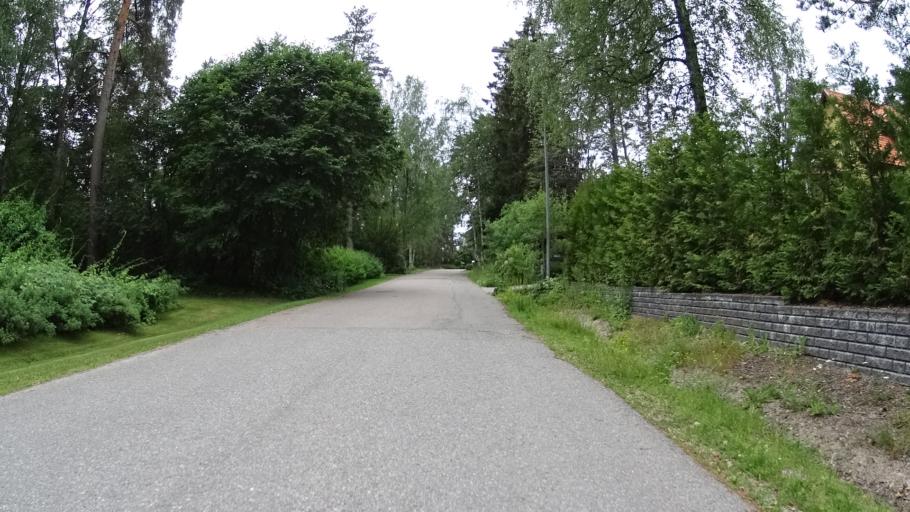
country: FI
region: Uusimaa
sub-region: Helsinki
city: Kauniainen
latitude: 60.2108
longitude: 24.7086
